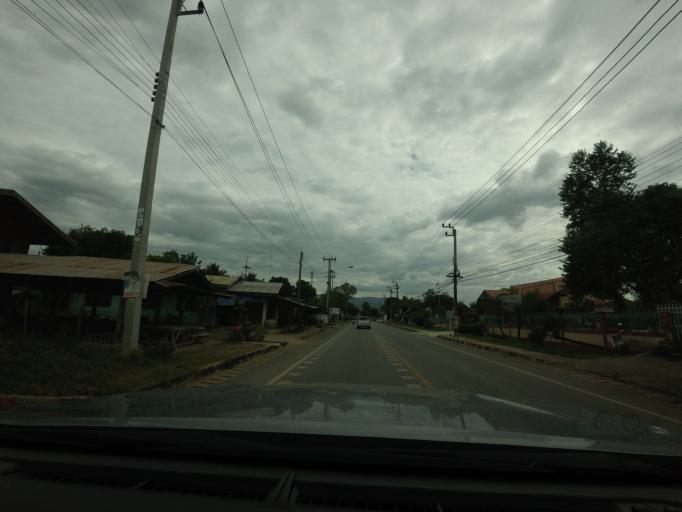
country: TH
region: Phitsanulok
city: Noen Maprang
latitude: 16.6776
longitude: 100.6113
